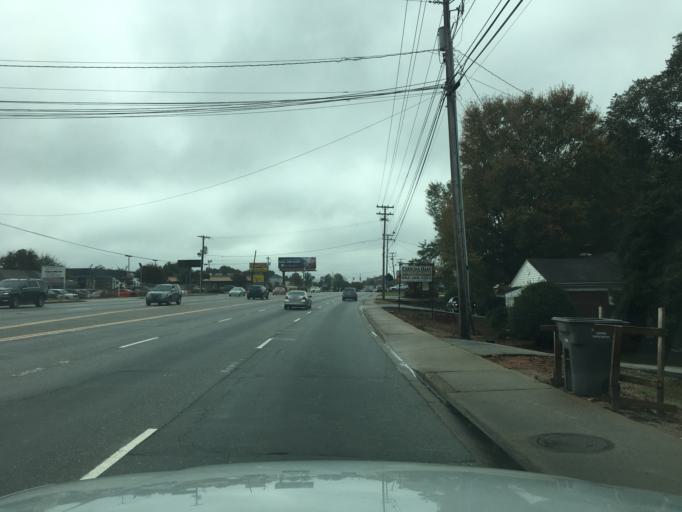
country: US
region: South Carolina
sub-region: Greenville County
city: Welcome
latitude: 34.8175
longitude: -82.4427
